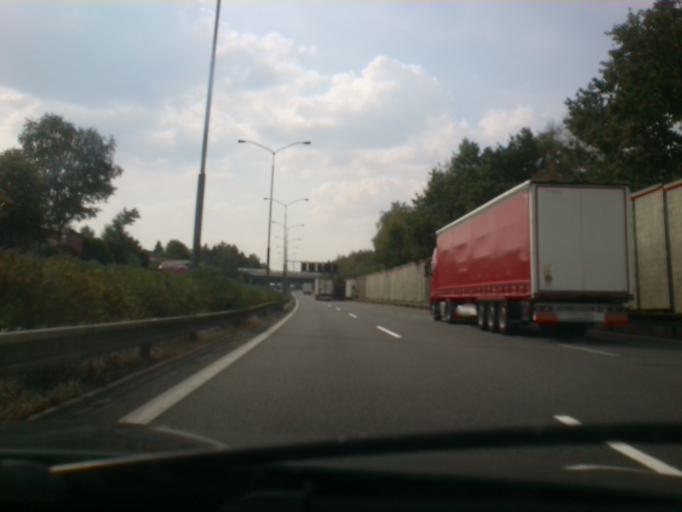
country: CZ
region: Central Bohemia
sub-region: Okres Praha-Vychod
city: Mnichovice
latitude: 49.9109
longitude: 14.7238
